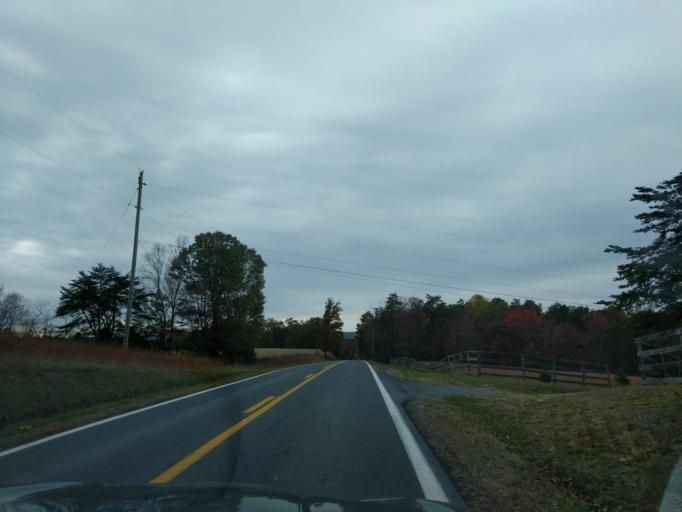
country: US
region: West Virginia
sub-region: Berkeley County
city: Inwood
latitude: 39.3912
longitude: -78.1723
